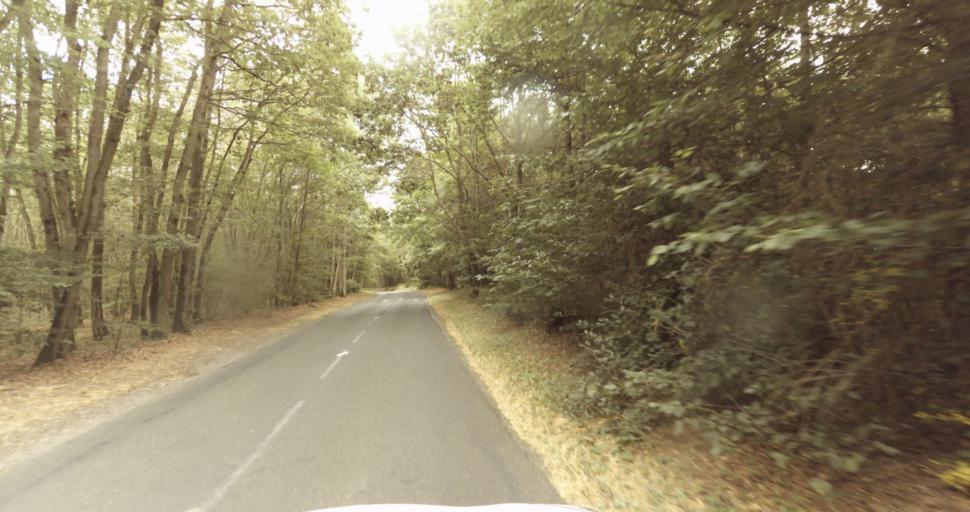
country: FR
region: Centre
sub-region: Departement d'Eure-et-Loir
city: Vert-en-Drouais
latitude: 48.7677
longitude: 1.3108
